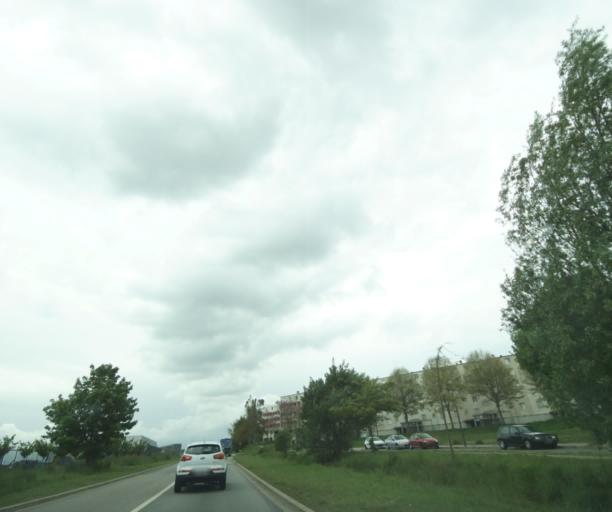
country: FR
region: Ile-de-France
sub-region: Departement des Yvelines
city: Ecquevilly
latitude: 48.9494
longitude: 1.9282
